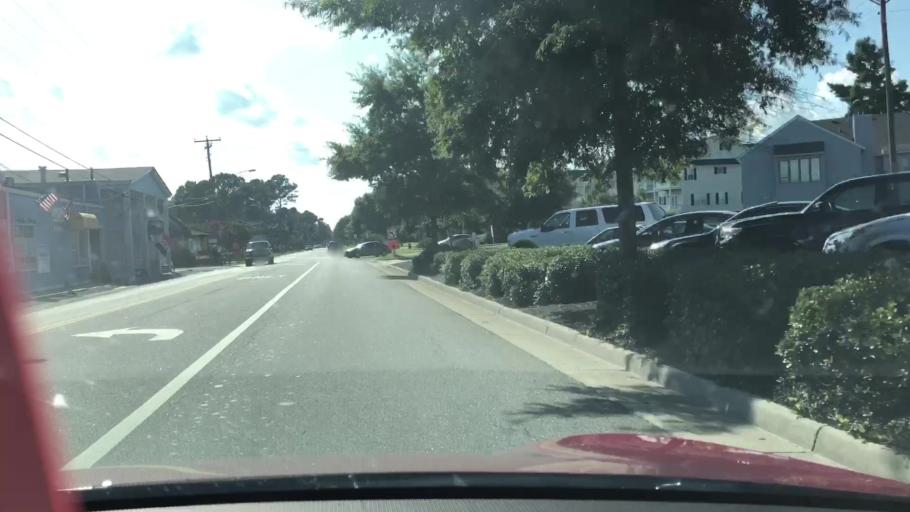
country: US
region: Virginia
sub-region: City of Virginia Beach
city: Virginia Beach
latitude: 36.8377
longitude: -75.9804
